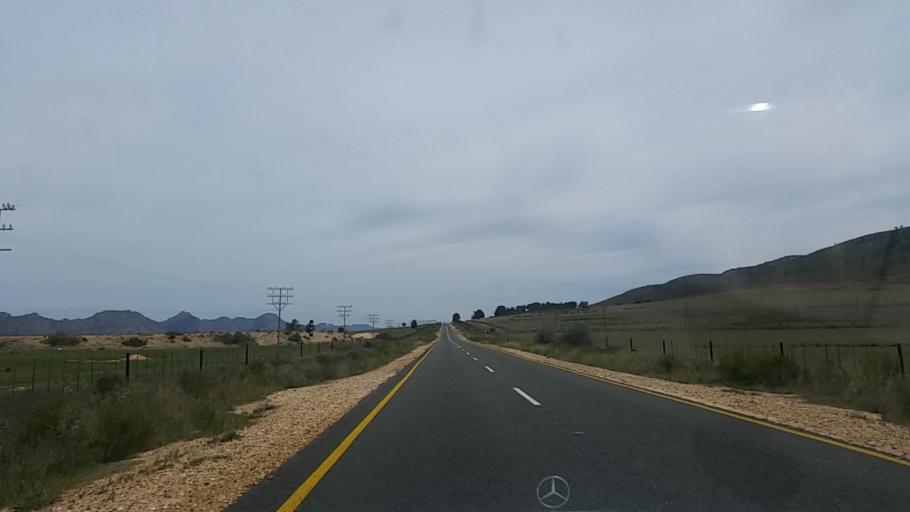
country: ZA
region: Western Cape
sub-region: Eden District Municipality
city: George
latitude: -33.7863
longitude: 22.6557
